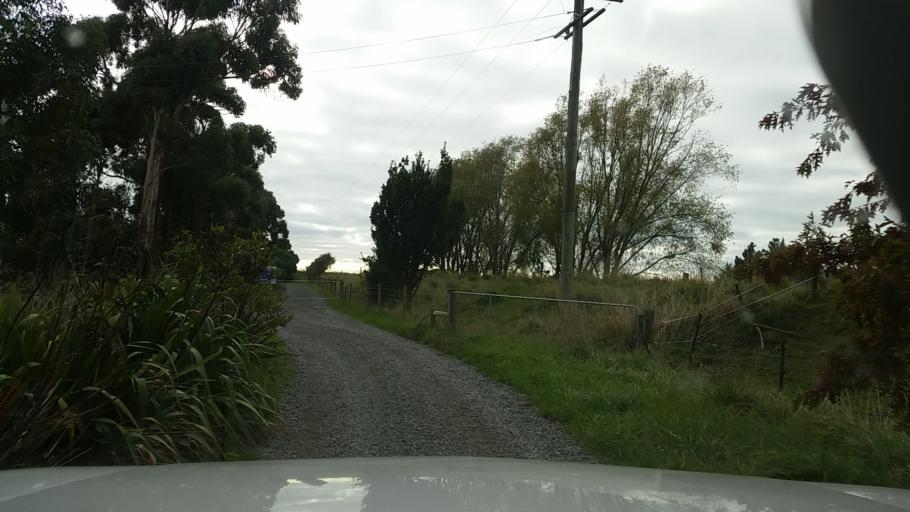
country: NZ
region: Marlborough
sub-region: Marlborough District
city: Blenheim
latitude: -41.5194
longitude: 174.0408
